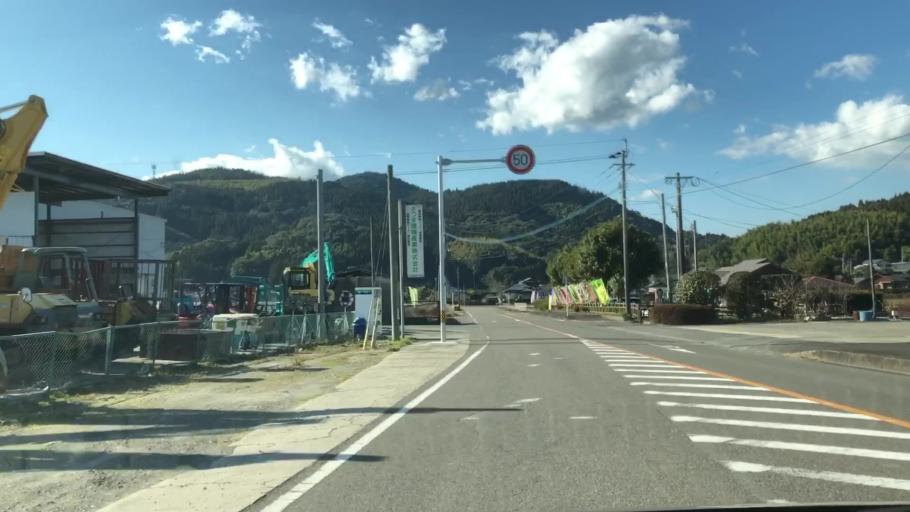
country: JP
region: Kagoshima
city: Satsumasendai
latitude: 31.8683
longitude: 130.4287
